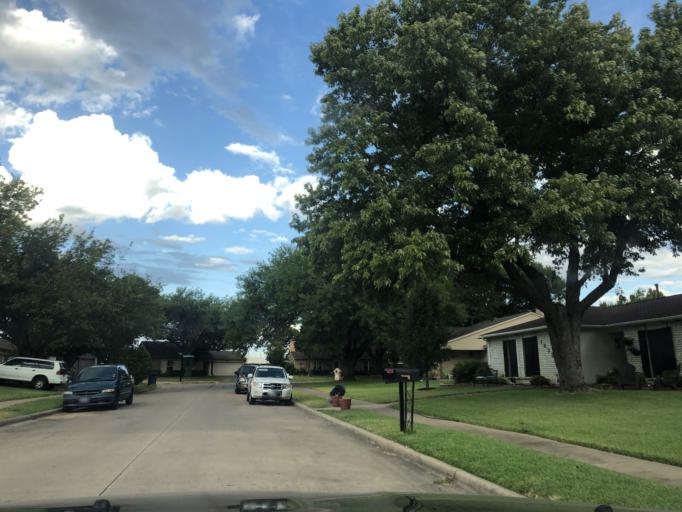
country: US
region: Texas
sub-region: Dallas County
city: Garland
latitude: 32.8720
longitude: -96.6558
